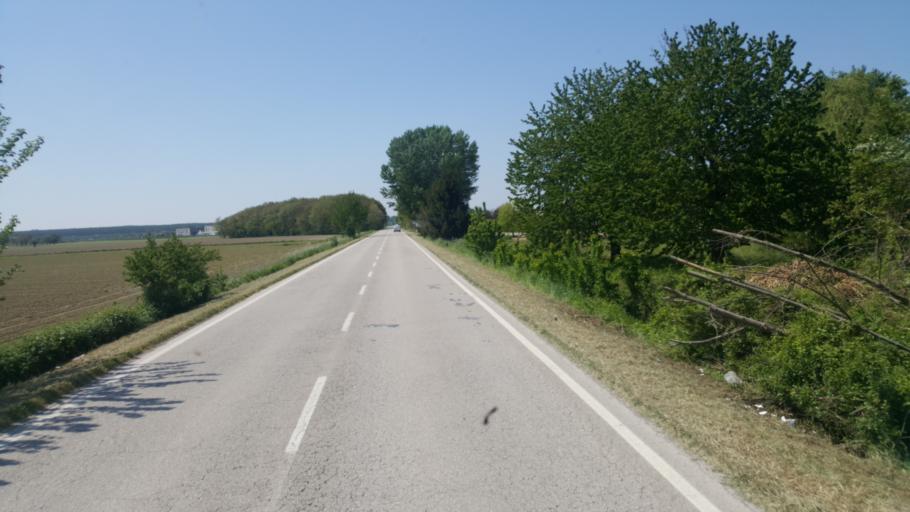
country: IT
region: Veneto
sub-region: Provincia di Rovigo
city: Ficarolo
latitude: 44.9495
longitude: 11.4448
